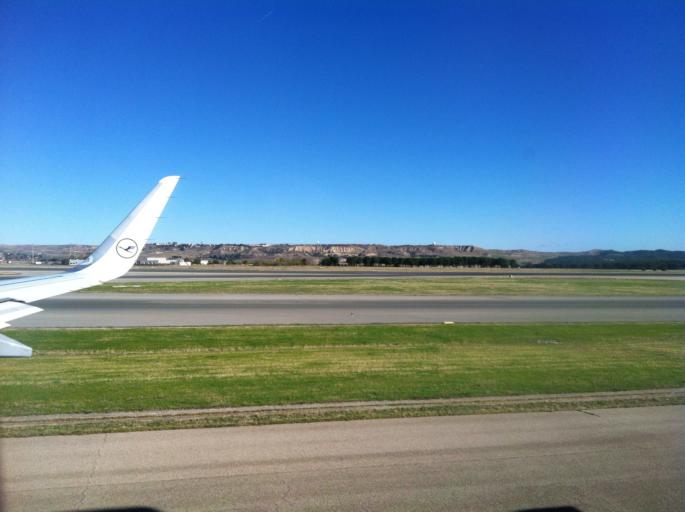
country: ES
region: Madrid
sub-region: Provincia de Madrid
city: Barajas de Madrid
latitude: 40.4805
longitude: -3.5754
